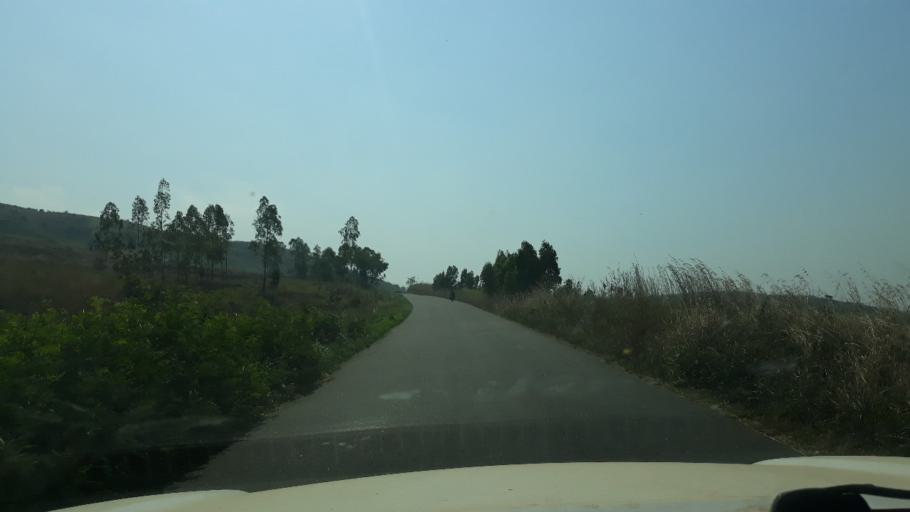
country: CD
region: South Kivu
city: Uvira
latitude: -3.2057
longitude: 29.1626
